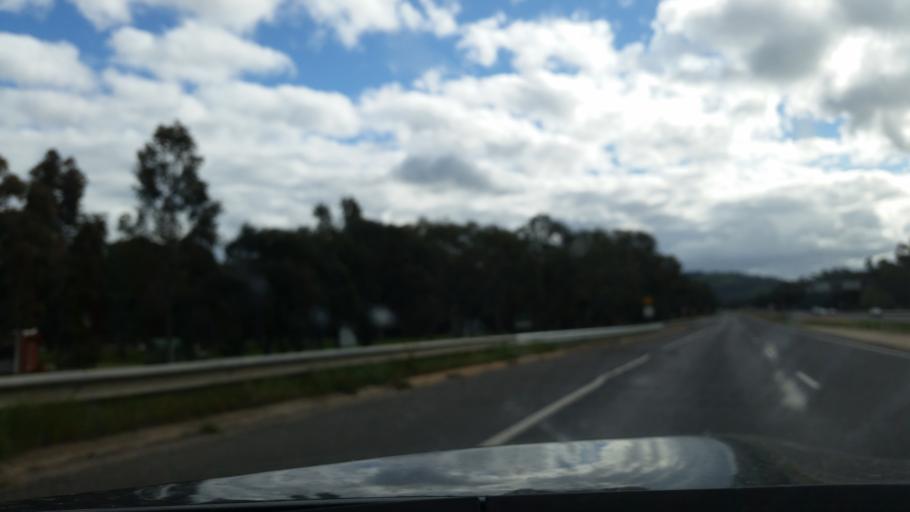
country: AU
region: Victoria
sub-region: Wodonga
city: Wodonga
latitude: -36.1093
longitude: 146.8563
